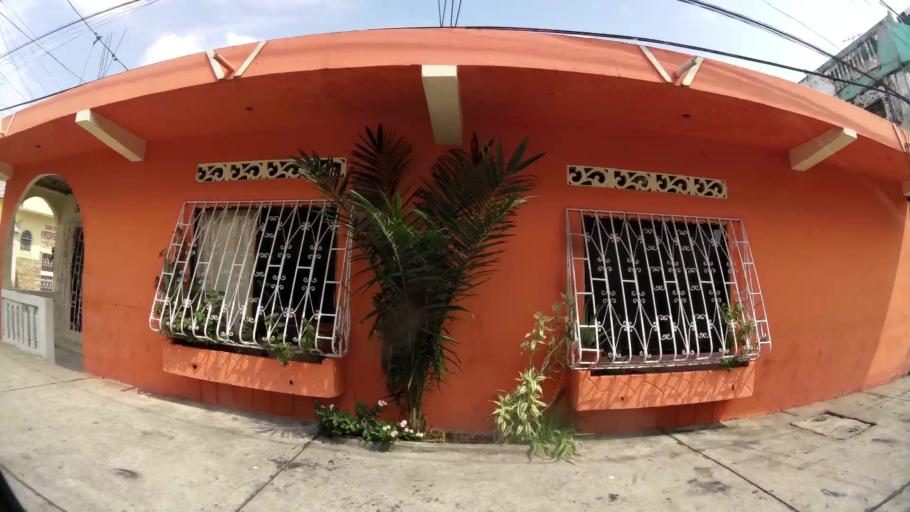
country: EC
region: Guayas
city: Guayaquil
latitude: -2.2610
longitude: -79.8834
